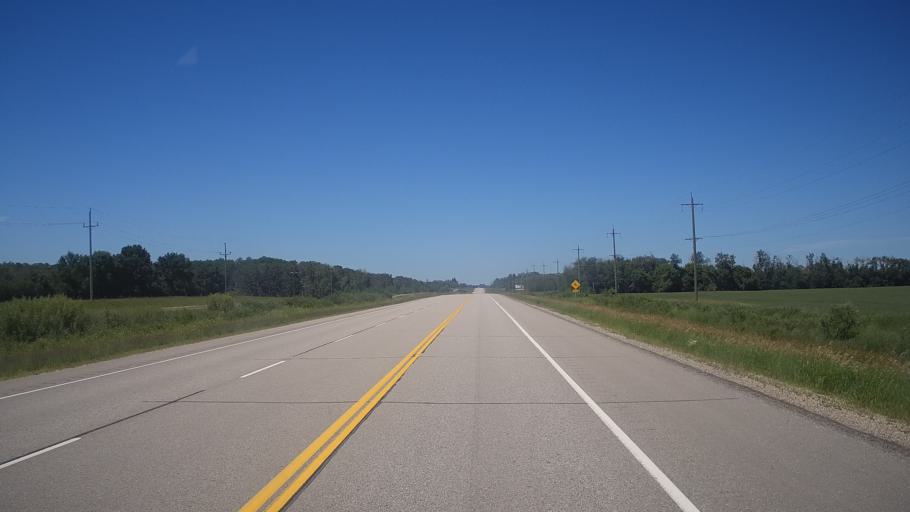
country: CA
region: Manitoba
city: Neepawa
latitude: 50.2253
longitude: -99.3465
